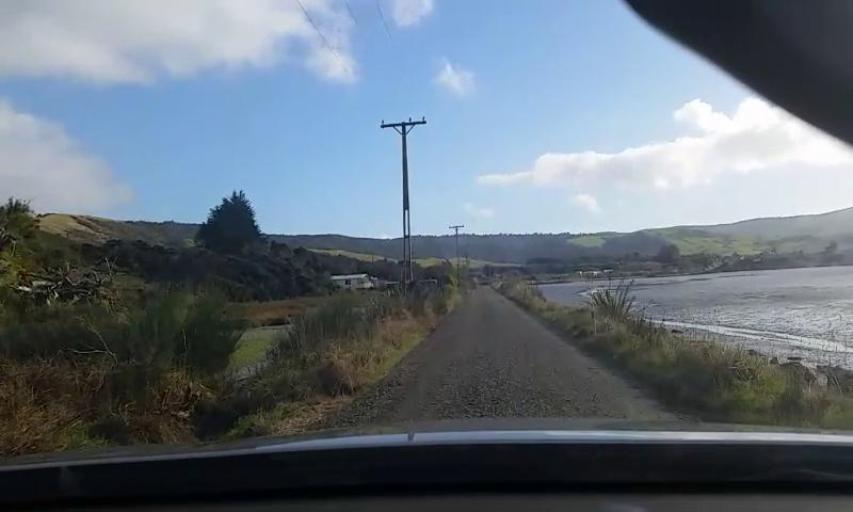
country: NZ
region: Otago
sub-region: Clutha District
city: Papatowai
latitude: -46.6297
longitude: 169.1400
